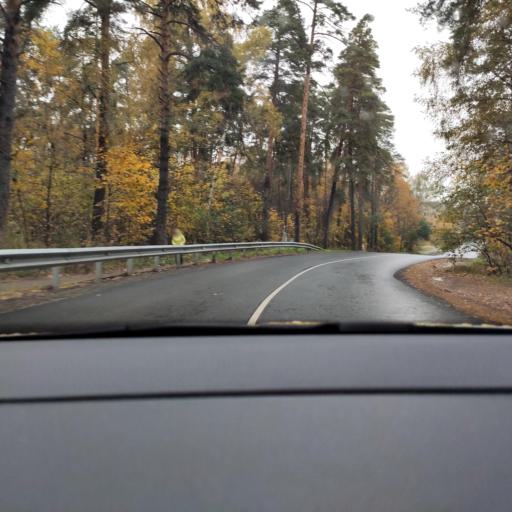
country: RU
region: Moskovskaya
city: Ivanteyevka
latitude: 55.9628
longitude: 37.9075
